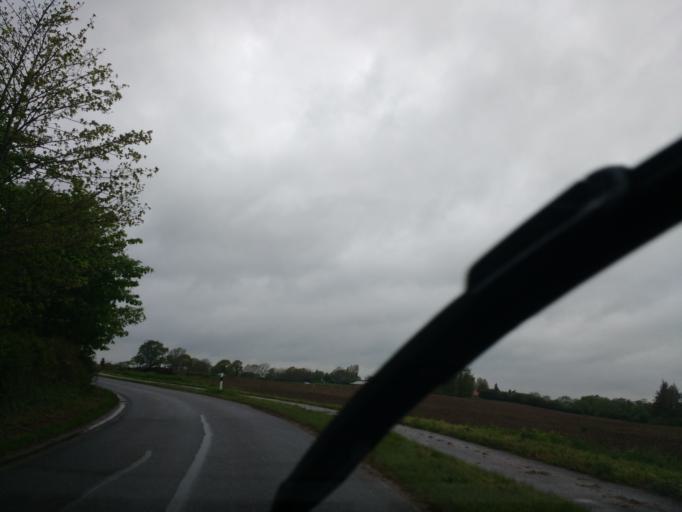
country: DE
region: Schleswig-Holstein
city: Waabs
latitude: 54.5230
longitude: 9.9716
